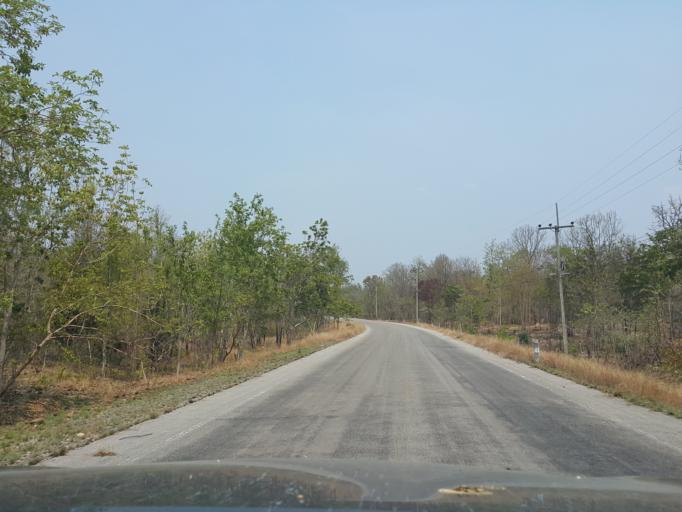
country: TH
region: Lampang
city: Mae Phrik
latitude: 17.5563
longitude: 99.1045
